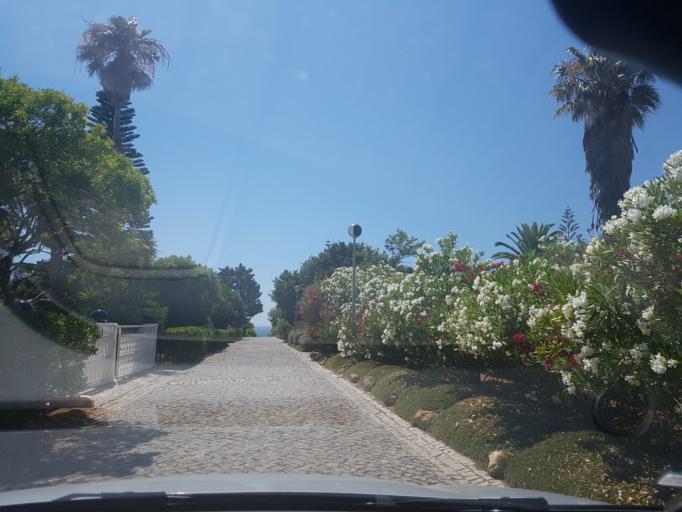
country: PT
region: Faro
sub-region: Lagoa
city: Carvoeiro
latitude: 37.0872
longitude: -8.4337
